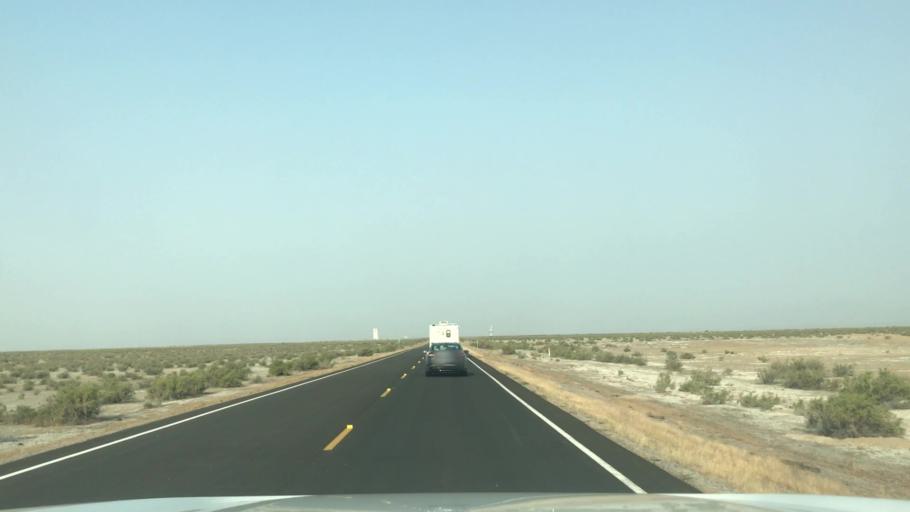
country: US
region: Utah
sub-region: Millard County
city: Delta
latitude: 39.3131
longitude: -112.7560
